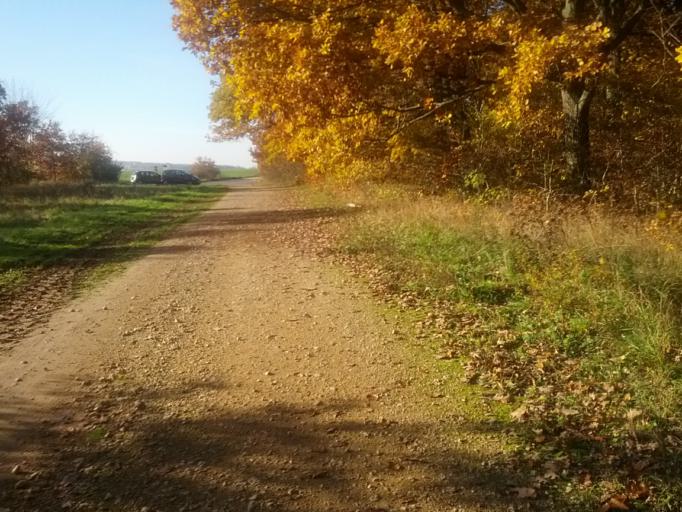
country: DE
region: Thuringia
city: Horselgau
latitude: 50.9599
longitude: 10.5992
